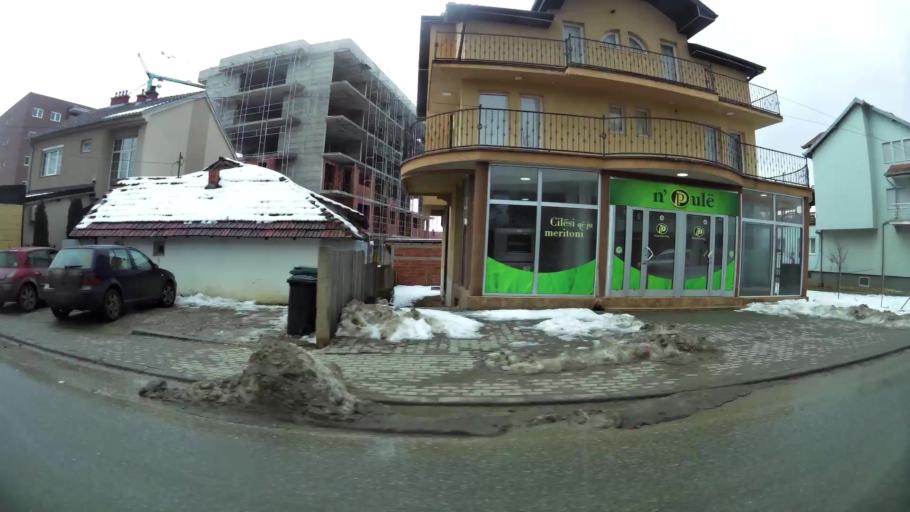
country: XK
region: Pristina
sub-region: Komuna e Prishtines
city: Pristina
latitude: 42.6546
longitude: 21.1901
